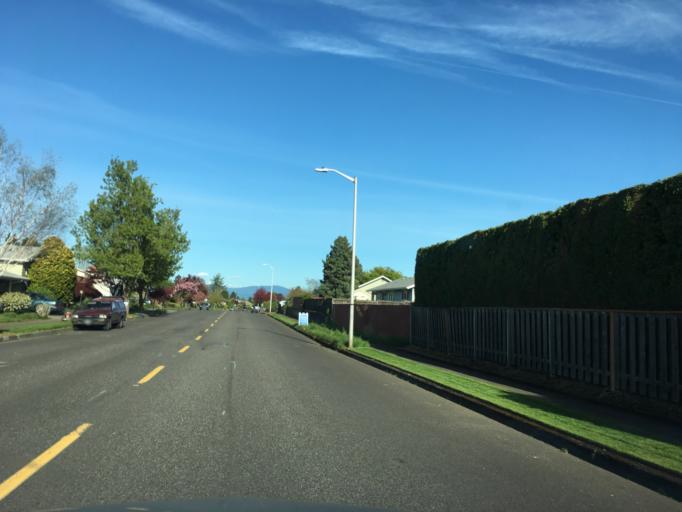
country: US
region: Oregon
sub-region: Multnomah County
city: Lents
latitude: 45.5478
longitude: -122.5199
